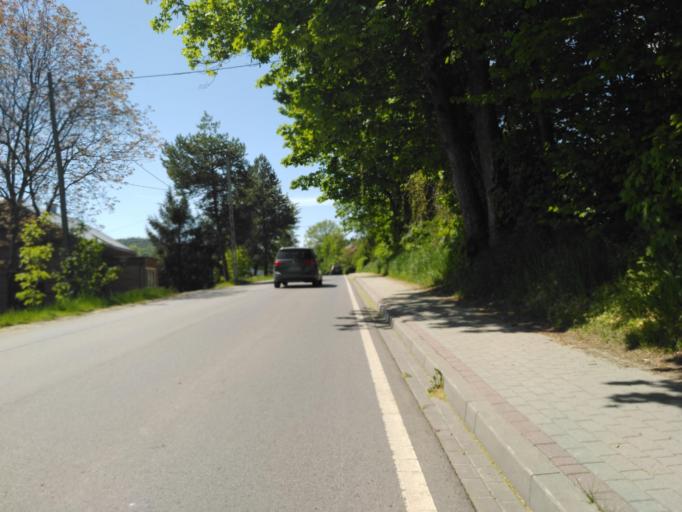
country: PL
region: Subcarpathian Voivodeship
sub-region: Powiat krosnienski
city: Iwonicz-Zdroj
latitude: 49.5754
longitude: 21.7936
